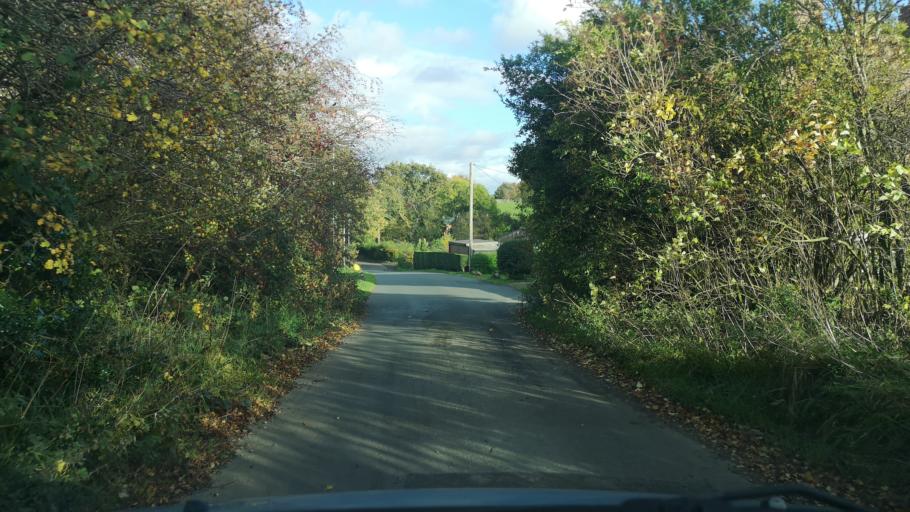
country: GB
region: England
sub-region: City and Borough of Wakefield
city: Middlestown
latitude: 53.6395
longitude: -1.6255
